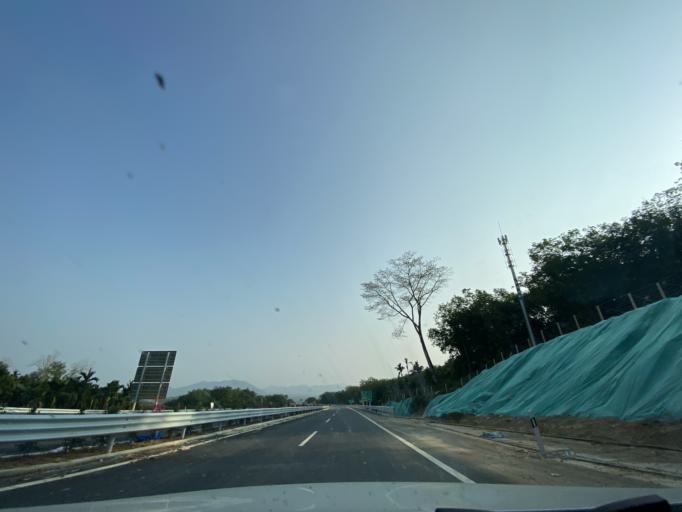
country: CN
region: Hainan
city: Xiangshui
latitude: 18.6448
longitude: 109.6293
